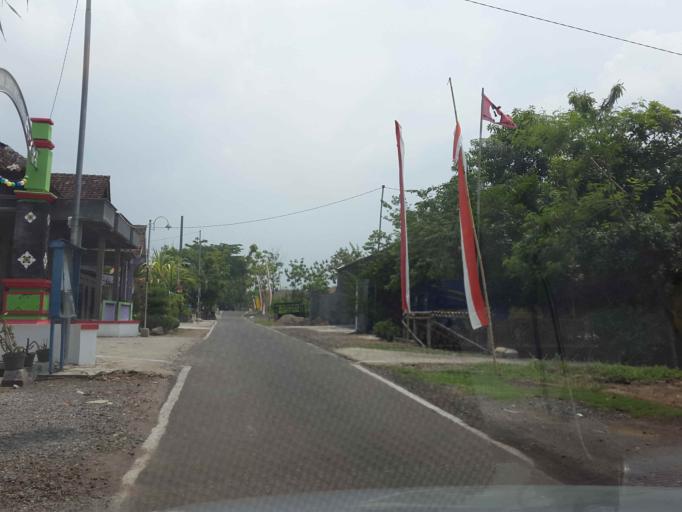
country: ID
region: Central Java
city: Jaten
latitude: -7.5972
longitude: 110.9192
